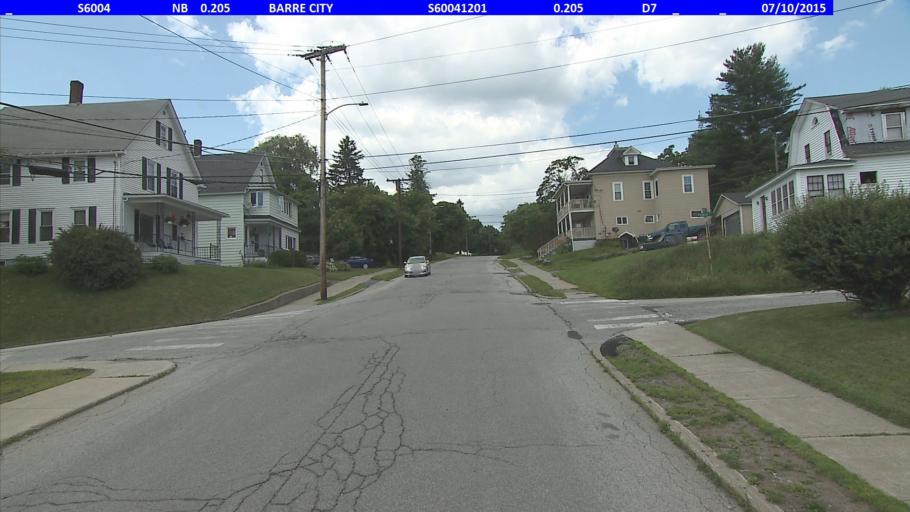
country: US
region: Vermont
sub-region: Washington County
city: Barre
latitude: 44.2086
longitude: -72.5113
